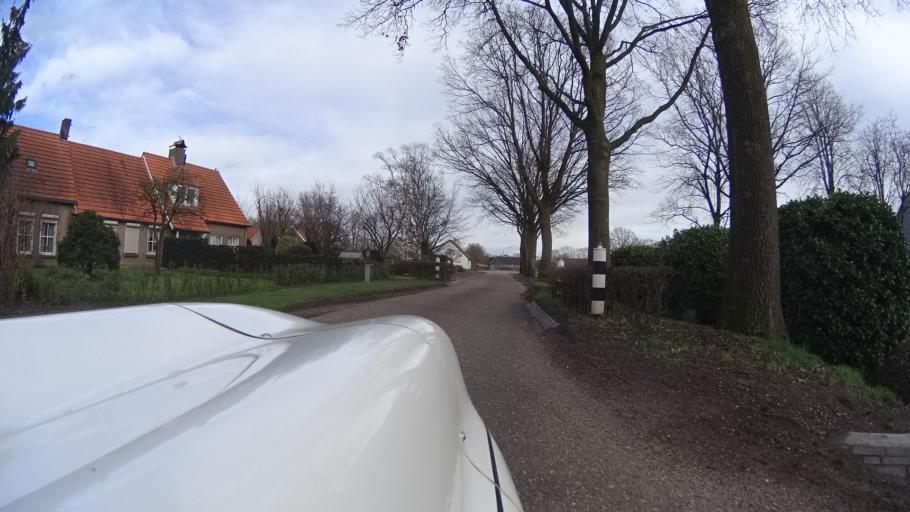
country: NL
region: North Brabant
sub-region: Gemeente Boekel
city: Boekel
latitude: 51.5975
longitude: 5.6634
